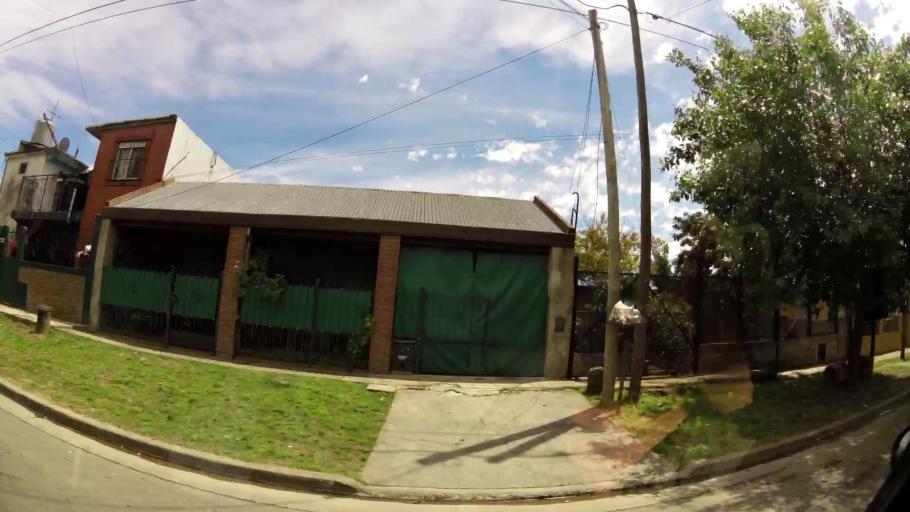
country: AR
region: Buenos Aires
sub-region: Partido de Quilmes
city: Quilmes
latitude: -34.7687
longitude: -58.2354
